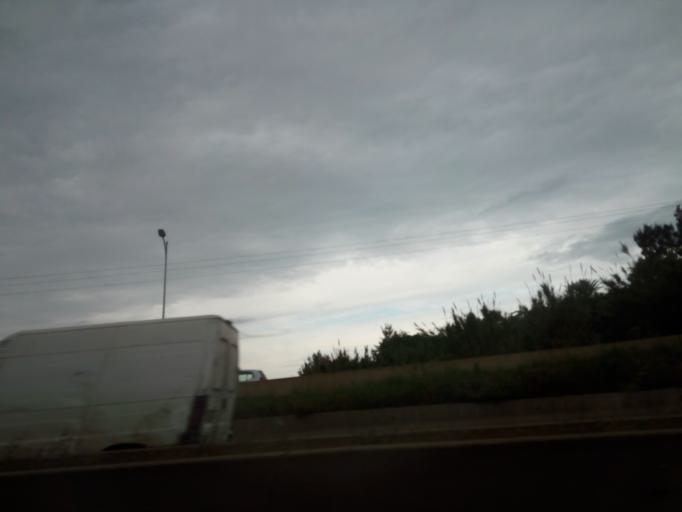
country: DZ
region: Tipaza
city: Cheraga
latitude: 36.7327
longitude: 2.9342
